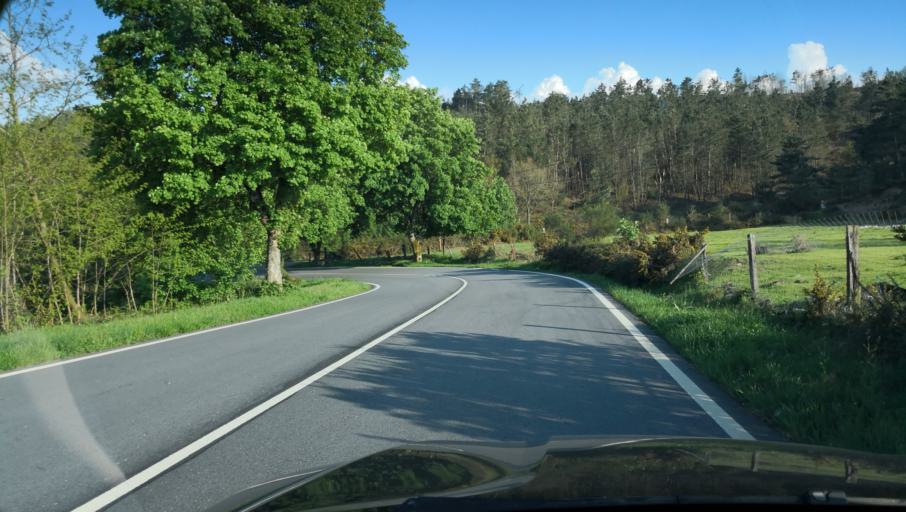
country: PT
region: Vila Real
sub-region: Santa Marta de Penaguiao
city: Santa Marta de Penaguiao
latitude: 41.2820
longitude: -7.8272
